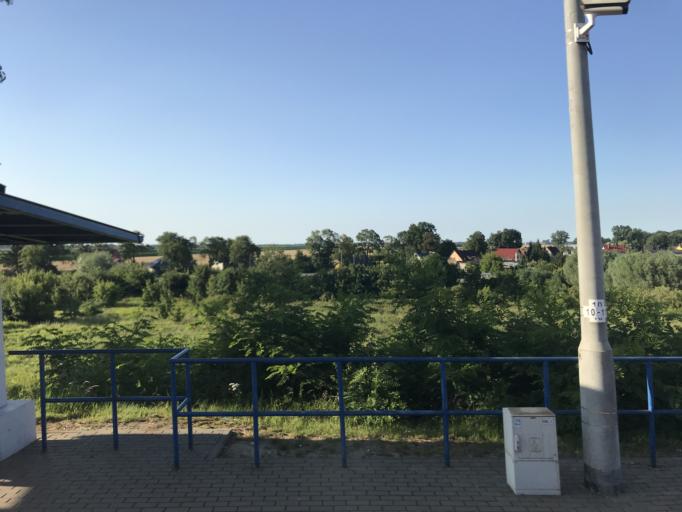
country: PL
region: Pomeranian Voivodeship
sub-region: Powiat malborski
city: Lisewo Malborskie
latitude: 54.0931
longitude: 18.8250
